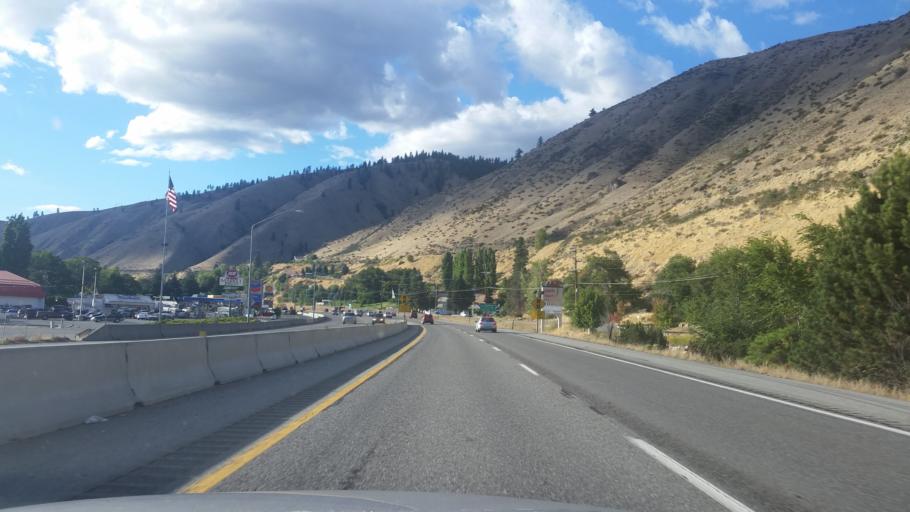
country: US
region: Washington
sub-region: Chelan County
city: Cashmere
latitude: 47.5174
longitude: -120.4510
